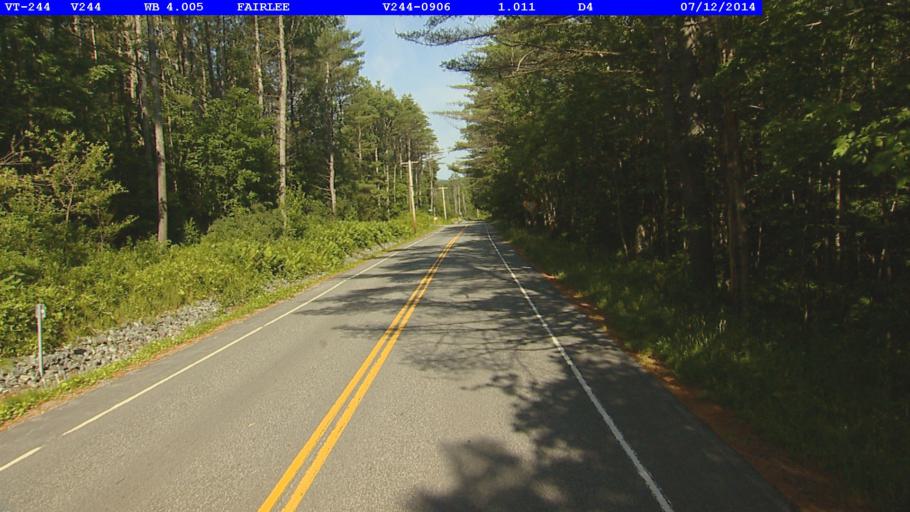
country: US
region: New Hampshire
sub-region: Grafton County
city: Orford
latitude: 43.8929
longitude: -72.2016
